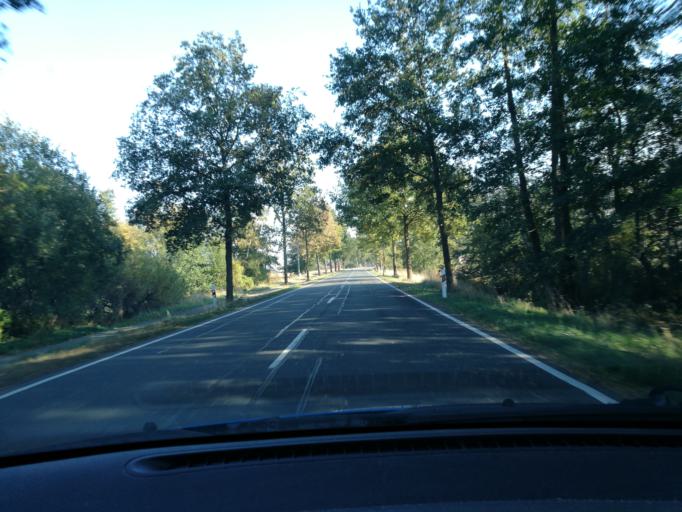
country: DE
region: Lower Saxony
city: Dannenberg
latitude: 53.0998
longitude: 11.0657
